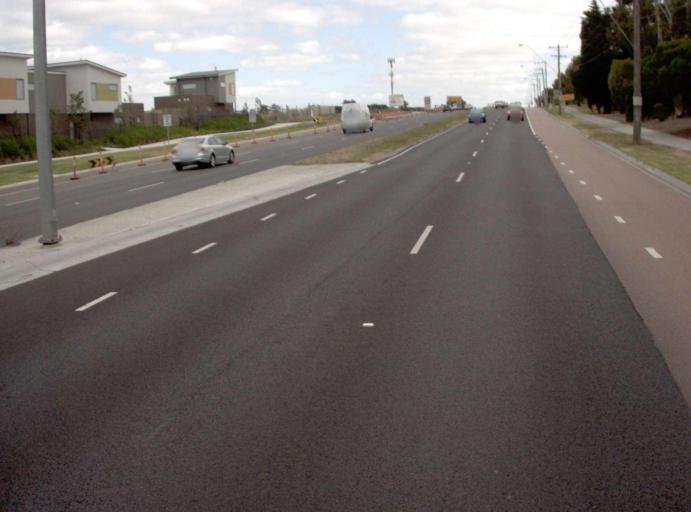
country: AU
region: Victoria
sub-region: Knox
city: Wantirna South
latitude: -37.8836
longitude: 145.2329
